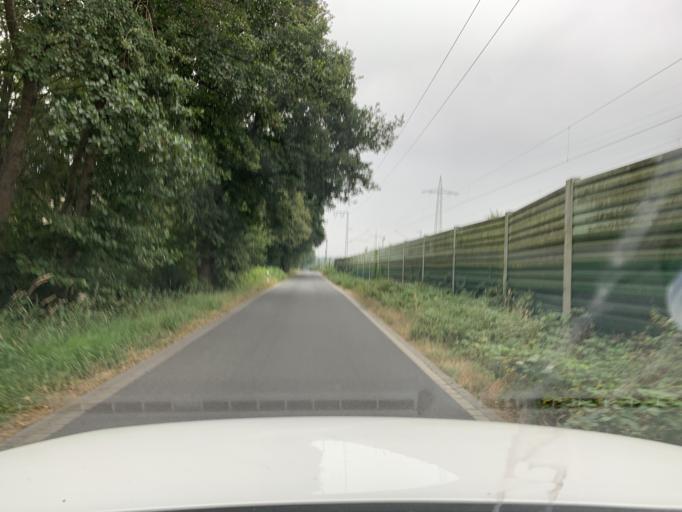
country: DE
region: North Rhine-Westphalia
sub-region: Regierungsbezirk Dusseldorf
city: Duisburg
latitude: 51.3871
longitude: 6.8107
